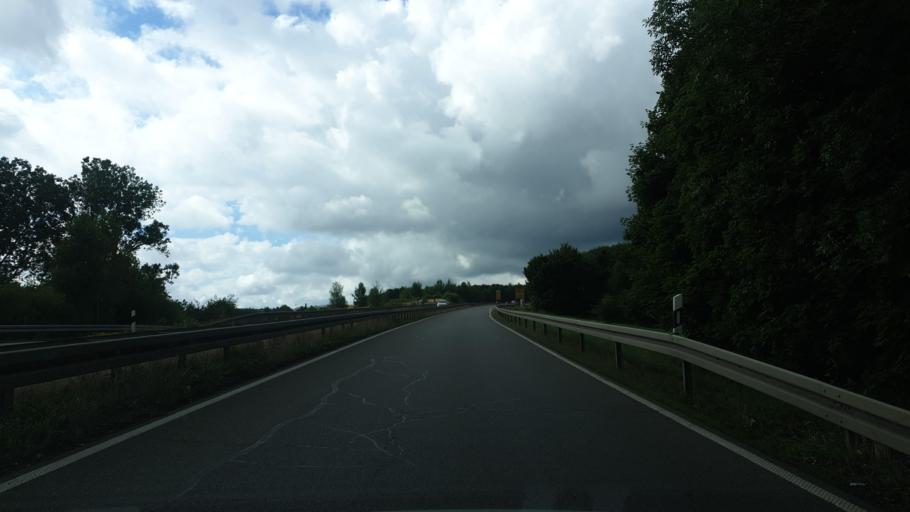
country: DE
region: Saxony
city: Reichenbach/Vogtland
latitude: 50.6113
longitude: 12.3150
